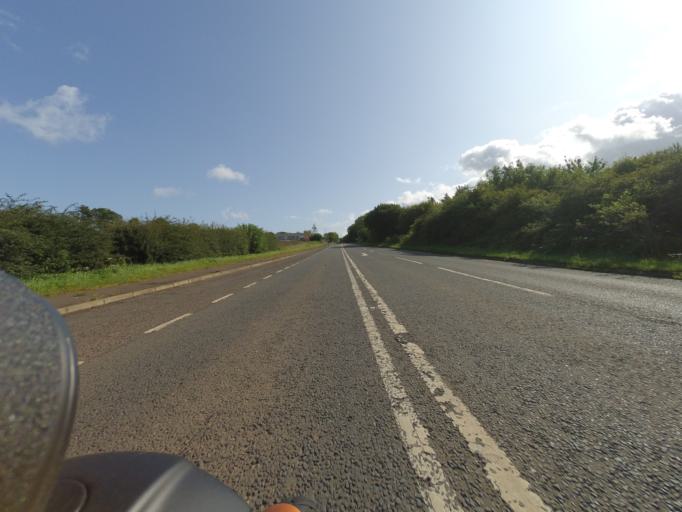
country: GB
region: Scotland
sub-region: East Lothian
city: East Linton
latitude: 55.9748
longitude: -2.7093
